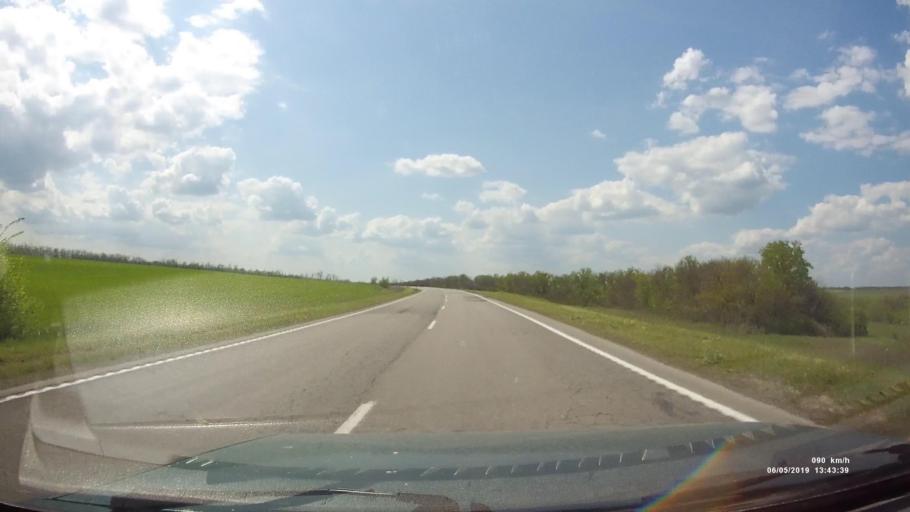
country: RU
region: Rostov
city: Semikarakorsk
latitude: 47.6608
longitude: 40.6341
